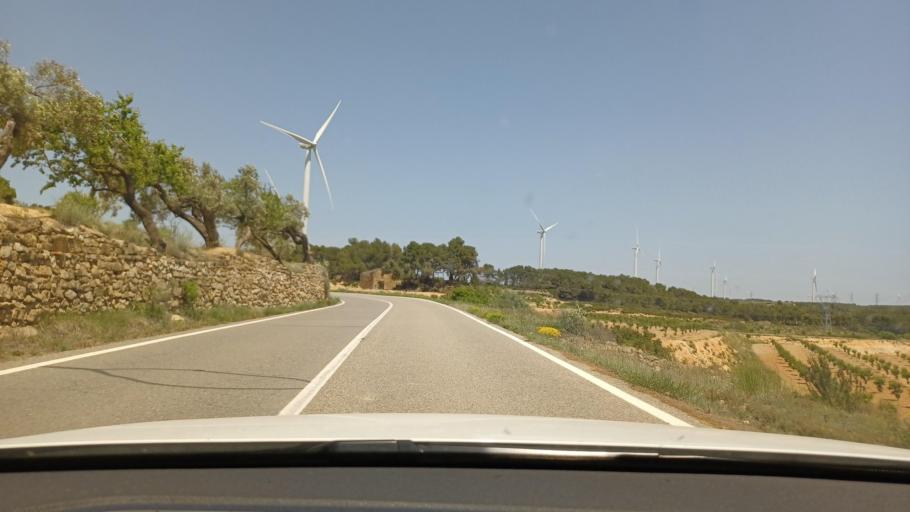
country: ES
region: Catalonia
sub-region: Provincia de Tarragona
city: Vilalba dels Arcs
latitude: 41.1030
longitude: 0.4175
